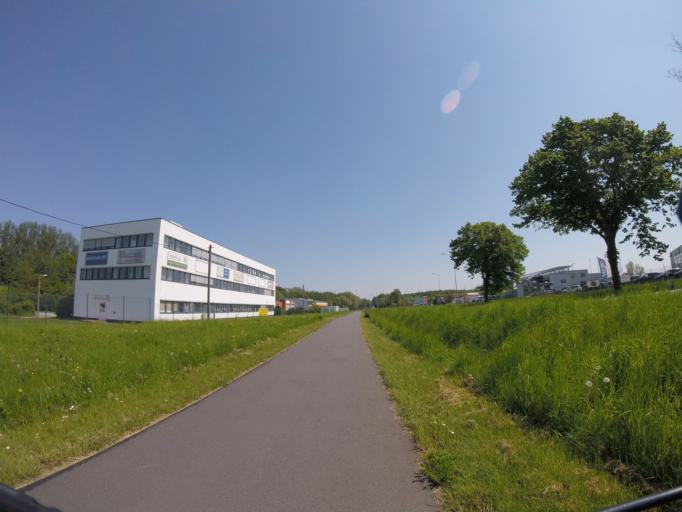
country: DE
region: Mecklenburg-Vorpommern
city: Bad Doberan
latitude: 54.1071
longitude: 11.9259
